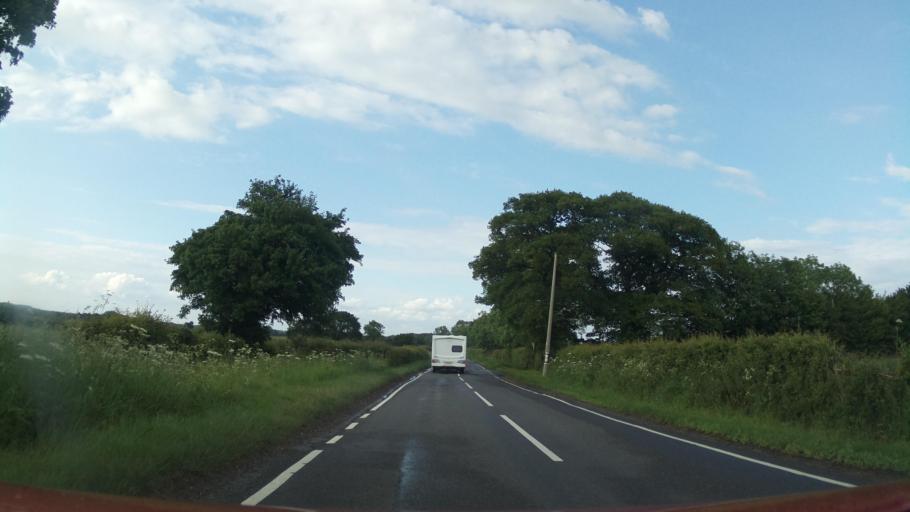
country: GB
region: England
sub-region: Lincolnshire
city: Great Gonerby
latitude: 53.0096
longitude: -0.6646
